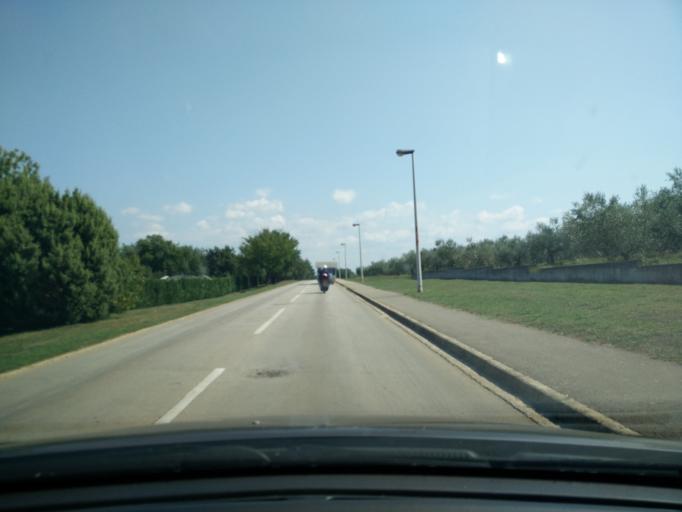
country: HR
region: Istarska
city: Novigrad
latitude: 45.2949
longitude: 13.5909
